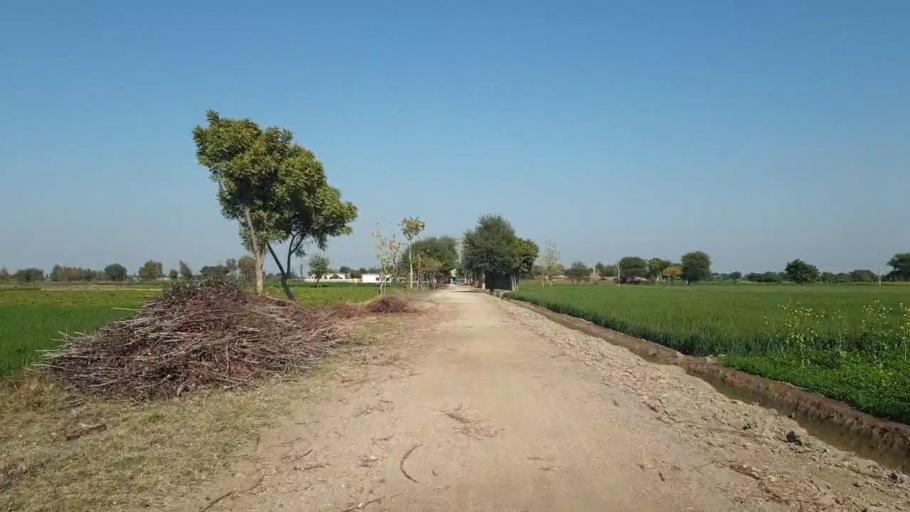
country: PK
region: Sindh
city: Shahdadpur
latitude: 25.9838
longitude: 68.6820
